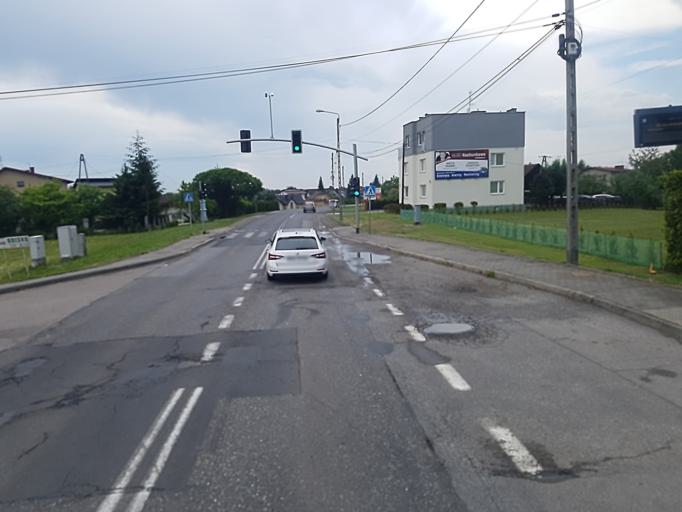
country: PL
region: Silesian Voivodeship
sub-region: Powiat wodzislawski
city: Mszana
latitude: 49.9768
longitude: 18.5246
